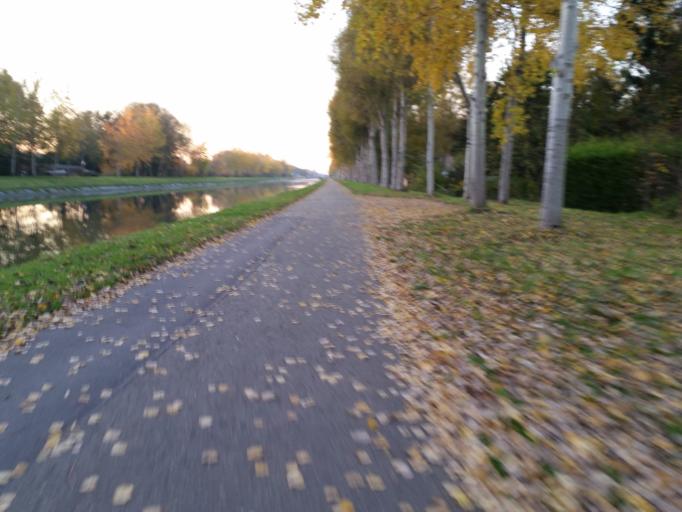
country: BE
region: Flanders
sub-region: Provincie Vlaams-Brabant
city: Boortmeerbeek
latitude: 50.9872
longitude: 4.5404
